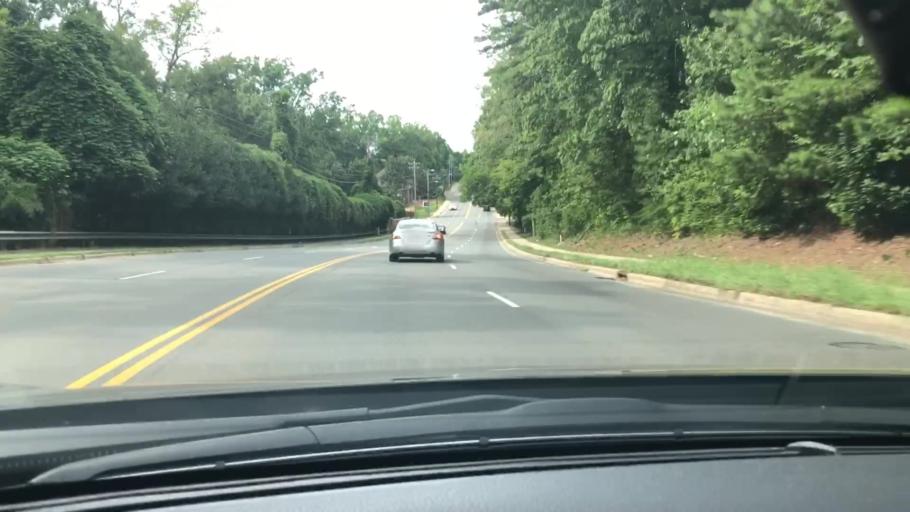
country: US
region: North Carolina
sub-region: Mecklenburg County
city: Charlotte
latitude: 35.1861
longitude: -80.8091
